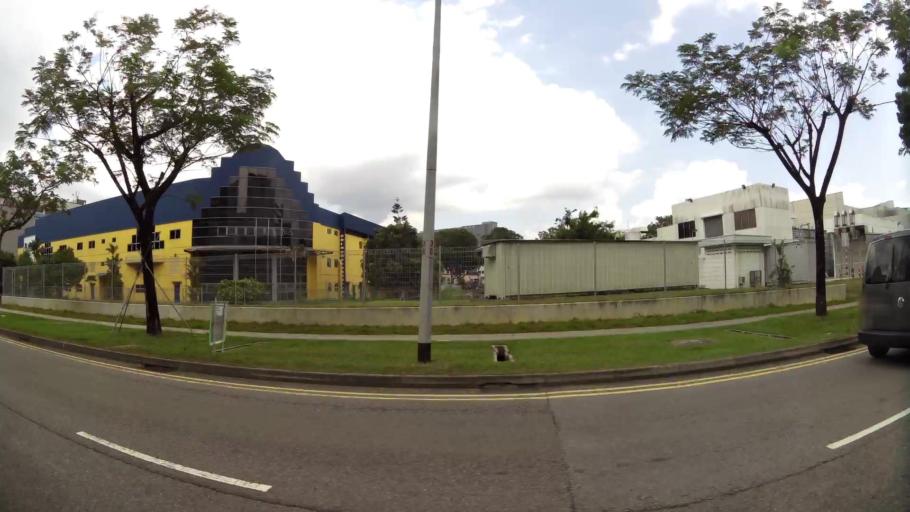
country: MY
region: Johor
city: Johor Bahru
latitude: 1.4467
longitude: 103.8067
